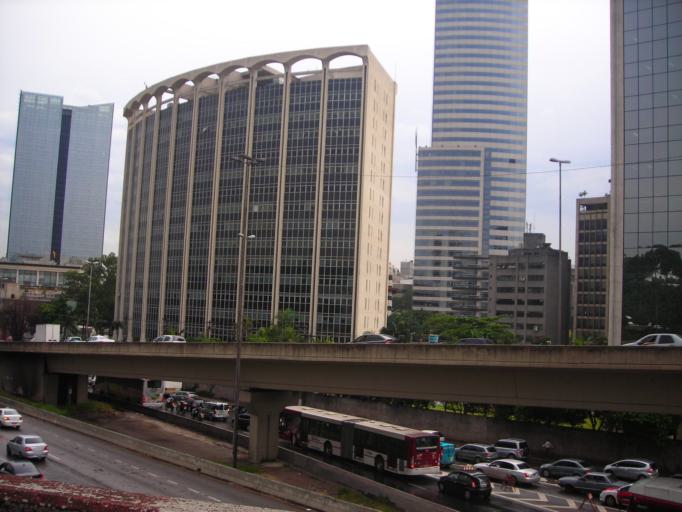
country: BR
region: Sao Paulo
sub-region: Sao Paulo
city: Sao Paulo
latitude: -23.5962
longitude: -46.6921
